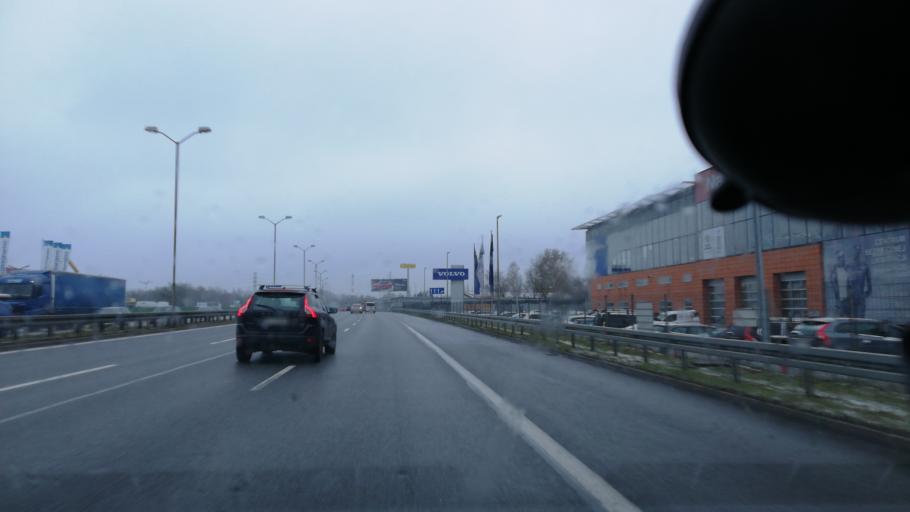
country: PL
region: Silesian Voivodeship
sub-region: Chorzow
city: Chorzow
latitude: 50.2789
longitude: 18.9543
